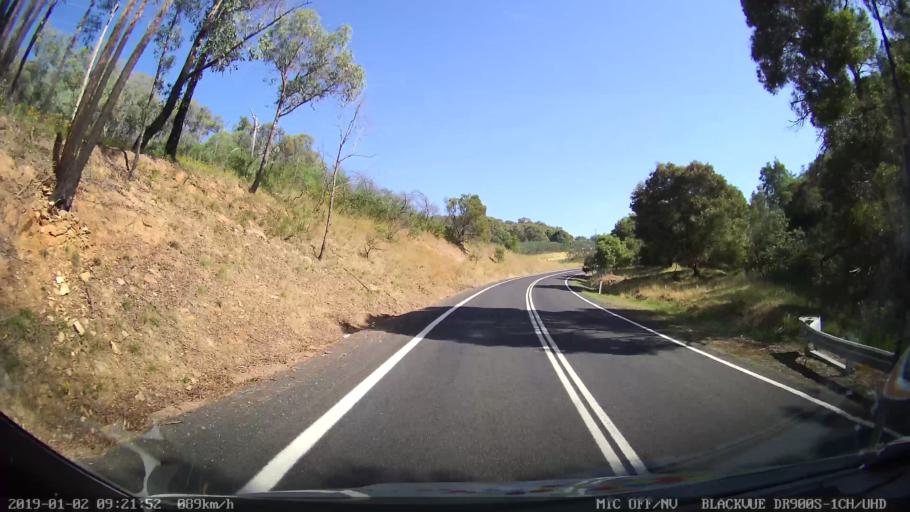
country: AU
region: New South Wales
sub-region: Tumut Shire
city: Tumut
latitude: -35.4008
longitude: 148.2892
